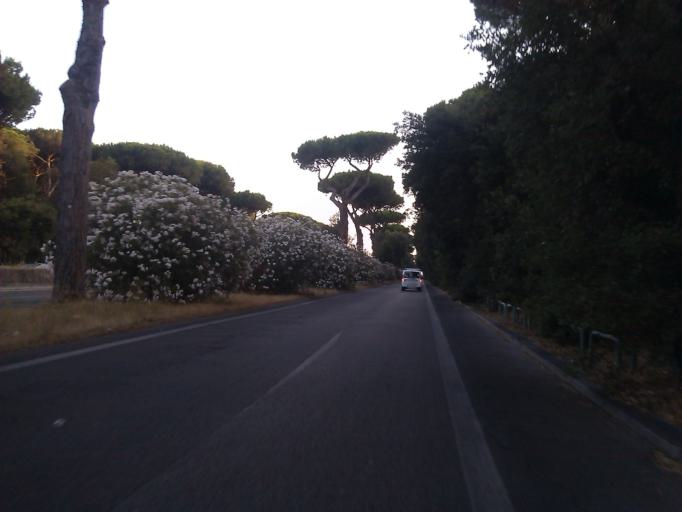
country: IT
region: Latium
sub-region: Citta metropolitana di Roma Capitale
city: Acilia-Castel Fusano-Ostia Antica
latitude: 41.7213
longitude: 12.3258
